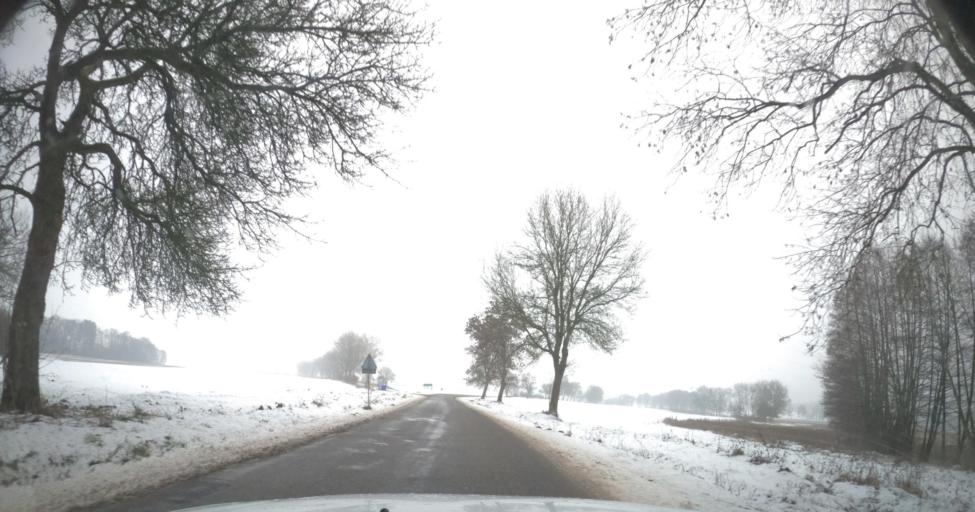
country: PL
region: West Pomeranian Voivodeship
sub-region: Powiat gryficki
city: Brojce
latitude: 53.8986
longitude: 15.3035
